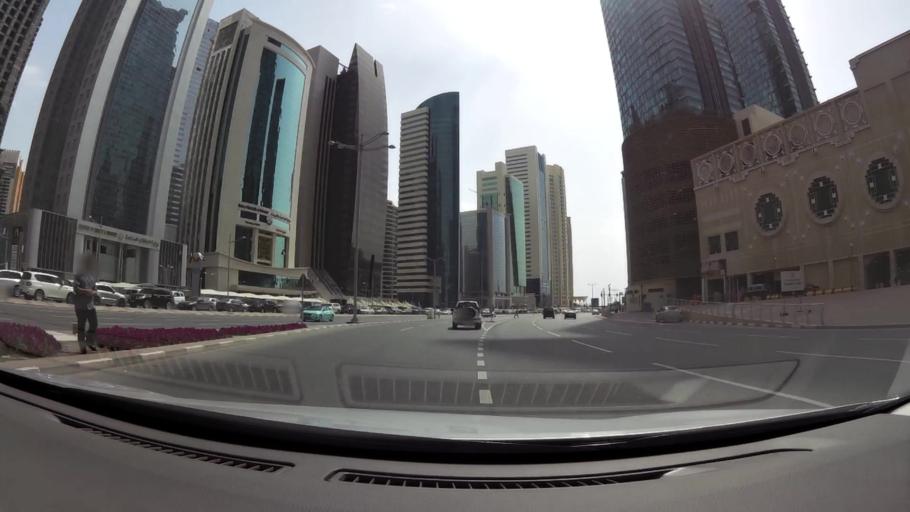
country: QA
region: Baladiyat ad Dawhah
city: Doha
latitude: 25.3260
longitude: 51.5322
